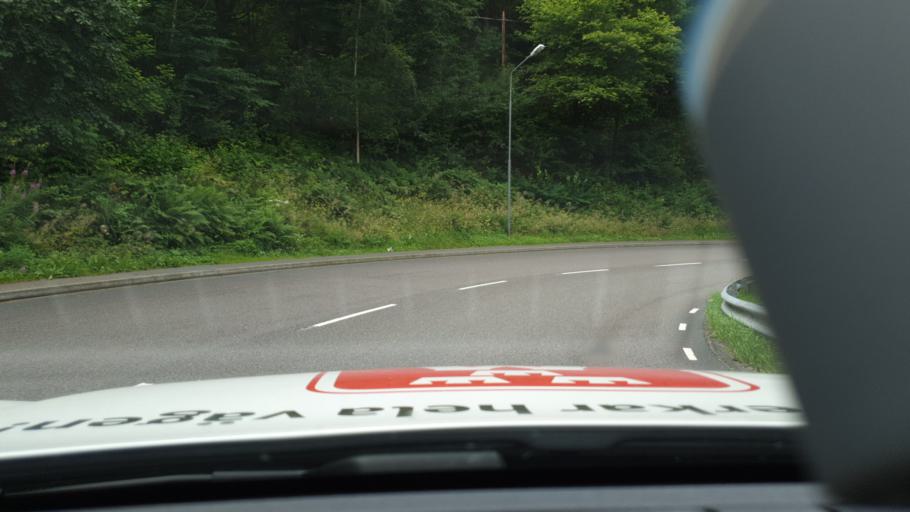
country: SE
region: Joenkoeping
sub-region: Jonkopings Kommun
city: Huskvarna
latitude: 57.7849
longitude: 14.2978
